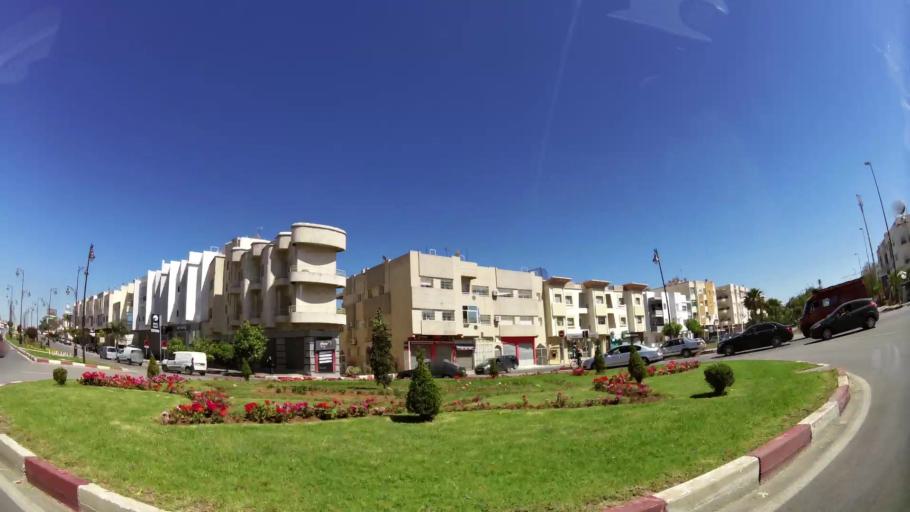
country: MA
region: Fes-Boulemane
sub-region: Fes
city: Fes
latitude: 34.0137
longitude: -5.0032
